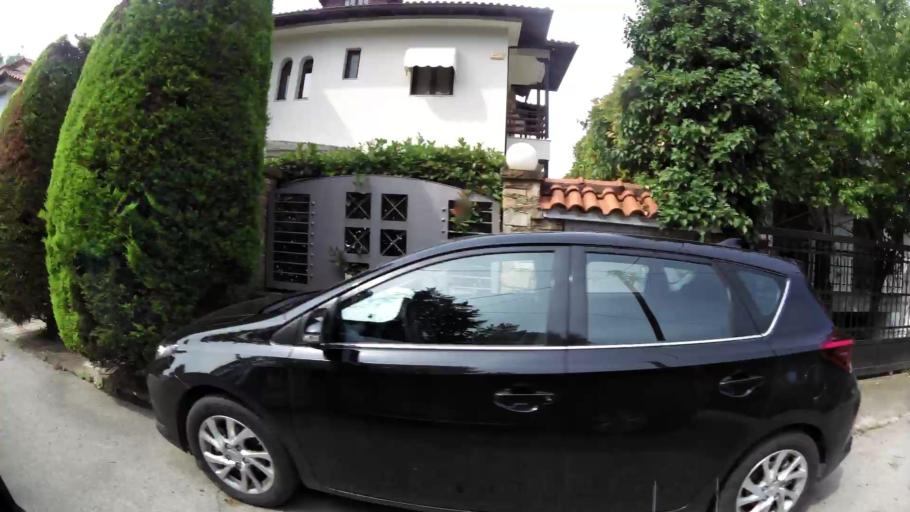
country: GR
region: Central Macedonia
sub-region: Nomos Thessalonikis
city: Panorama
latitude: 40.5820
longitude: 23.0301
